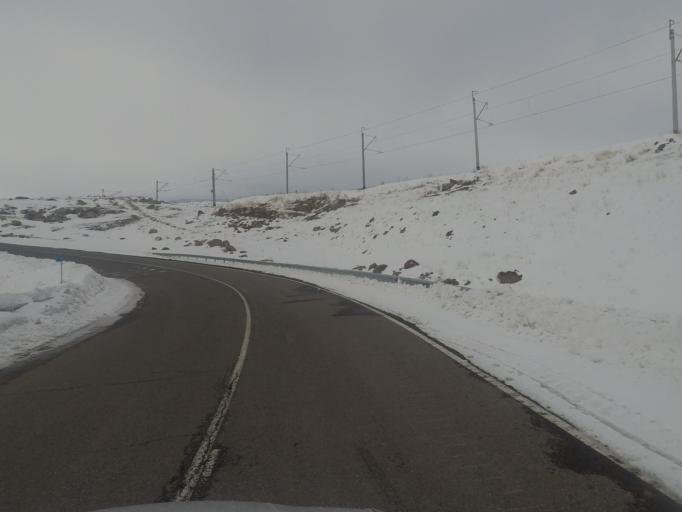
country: GE
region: Kvemo Kartli
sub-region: Tsalka
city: Tsalka
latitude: 41.4514
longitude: 43.8545
